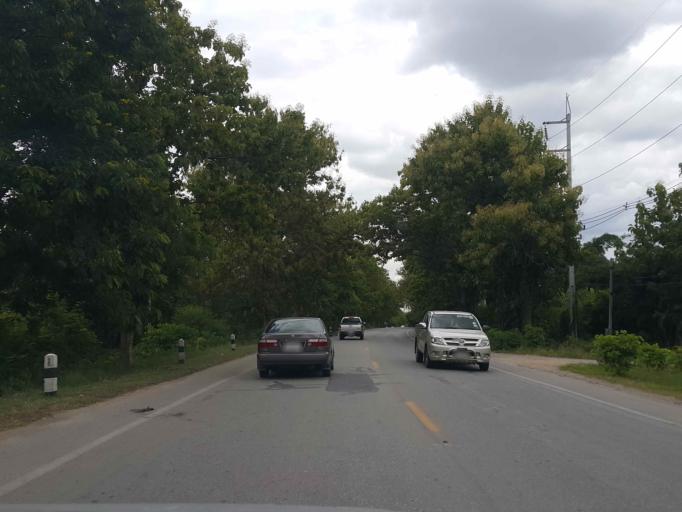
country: TH
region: Chiang Mai
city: Doi Lo
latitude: 18.4374
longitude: 98.8743
